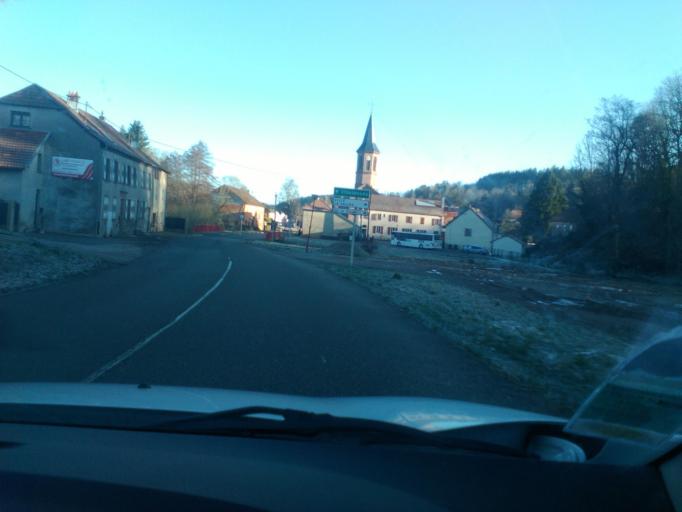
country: FR
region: Alsace
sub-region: Departement du Haut-Rhin
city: Sainte-Marie-aux-Mines
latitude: 48.3574
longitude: 7.1344
